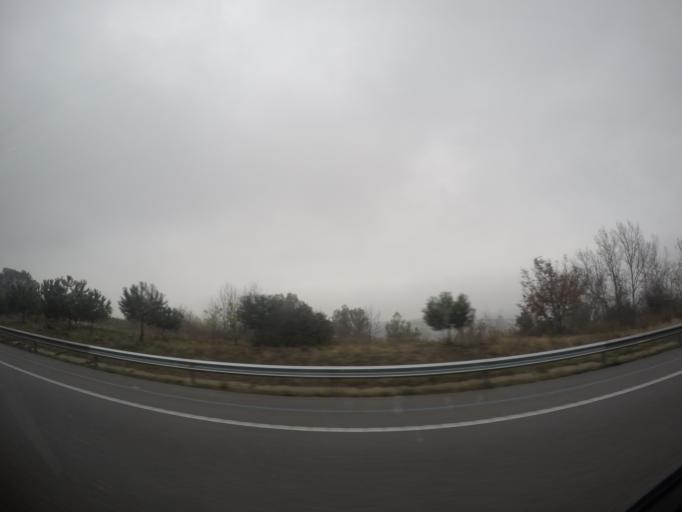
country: ES
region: Catalonia
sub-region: Provincia de Barcelona
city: Castellvi de Rosanes
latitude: 41.4512
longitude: 1.8790
